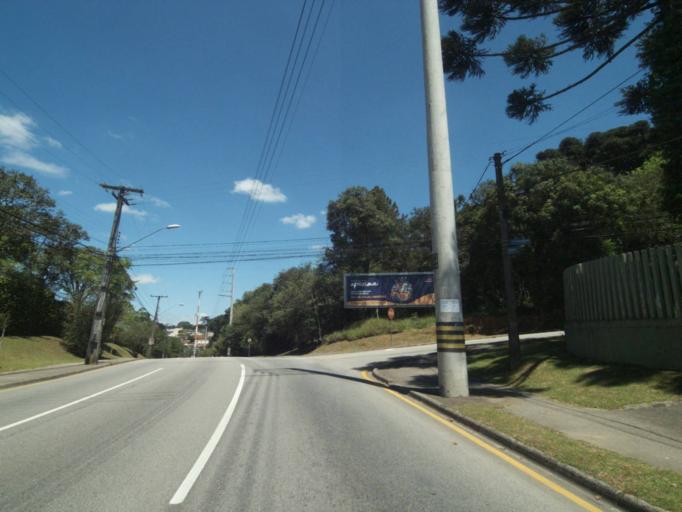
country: BR
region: Parana
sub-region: Curitiba
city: Curitiba
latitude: -25.3963
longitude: -49.2735
